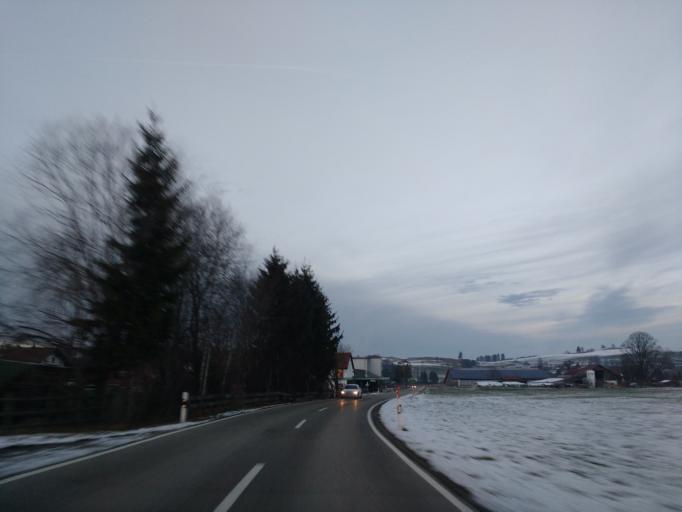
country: DE
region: Bavaria
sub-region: Swabia
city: Halblech
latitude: 47.6399
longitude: 10.8167
